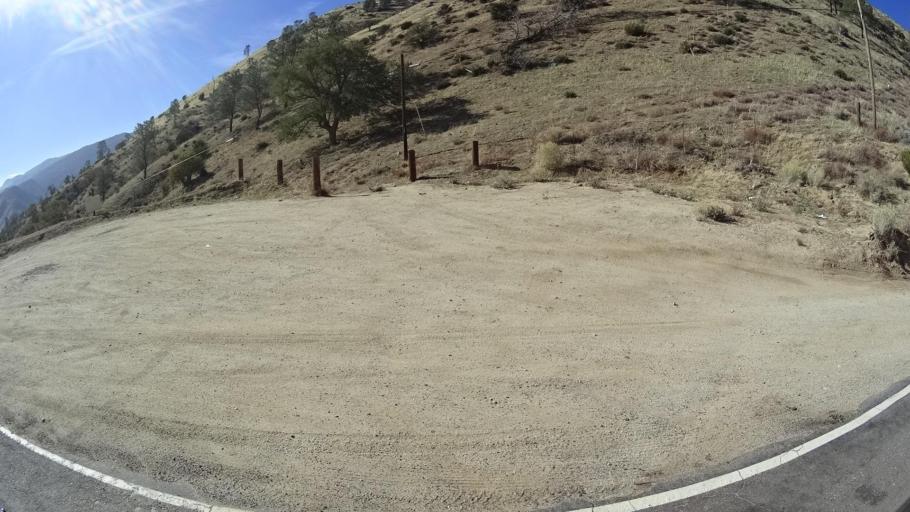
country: US
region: California
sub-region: Kern County
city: Bodfish
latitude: 35.5690
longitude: -118.5069
